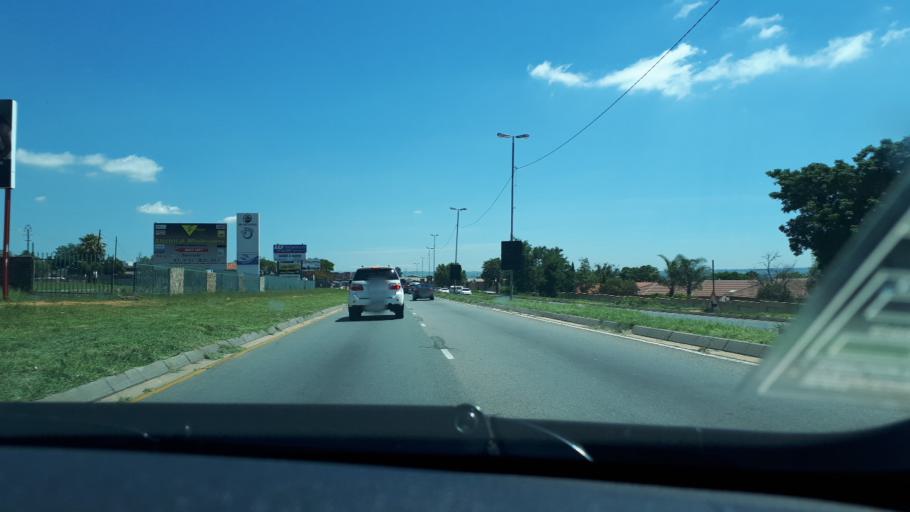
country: ZA
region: Gauteng
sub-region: West Rand District Municipality
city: Muldersdriseloop
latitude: -26.0511
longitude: 27.9561
